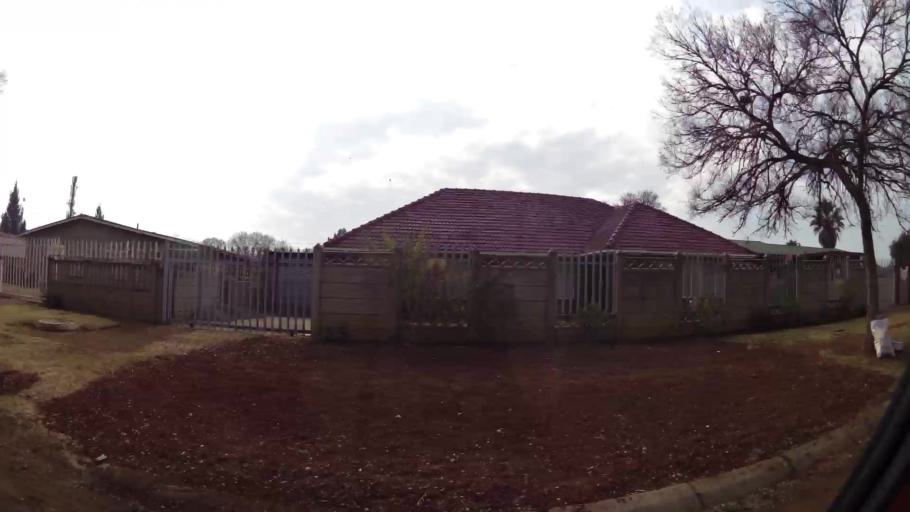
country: ZA
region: Gauteng
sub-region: Sedibeng District Municipality
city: Vanderbijlpark
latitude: -26.6917
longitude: 27.8429
